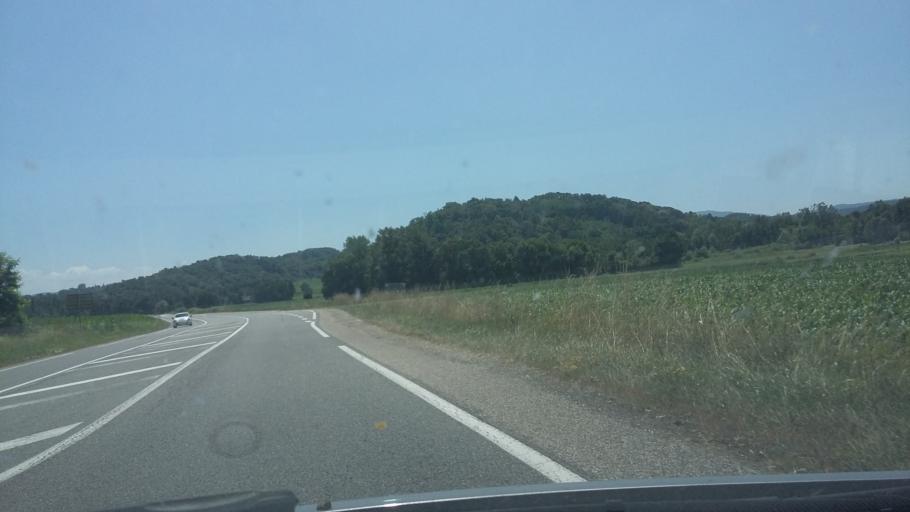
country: FR
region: Rhone-Alpes
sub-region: Departement de l'Ain
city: Belley
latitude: 45.7934
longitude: 5.6827
